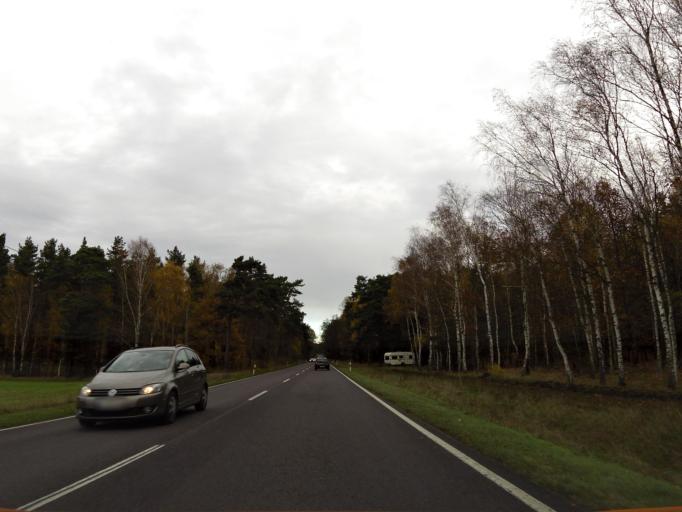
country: DE
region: Saxony-Anhalt
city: Letzlingen
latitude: 52.4168
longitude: 11.4803
